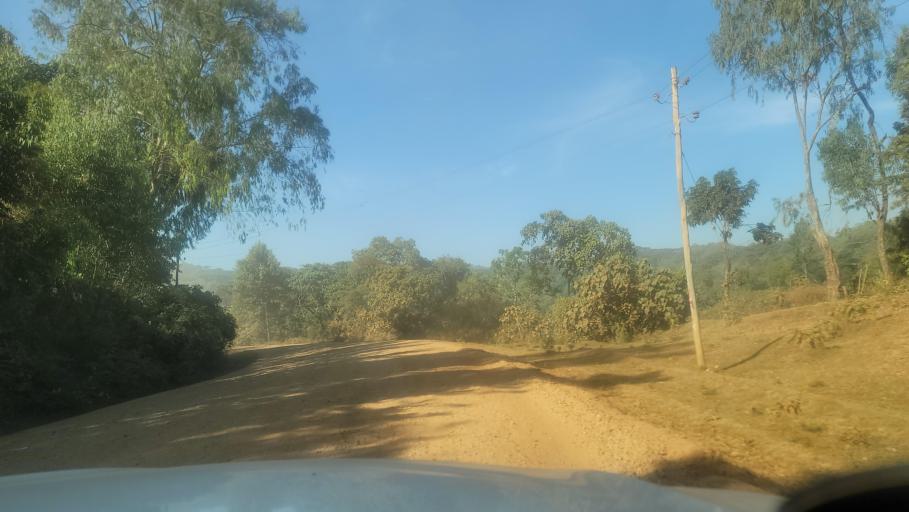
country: ET
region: Oromiya
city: Agaro
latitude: 7.8381
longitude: 36.5550
